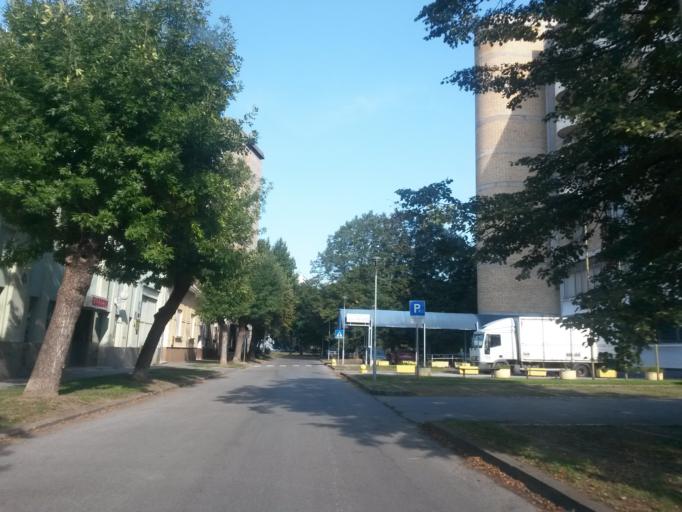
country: HR
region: Osjecko-Baranjska
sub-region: Grad Osijek
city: Osijek
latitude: 45.5541
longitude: 18.6936
